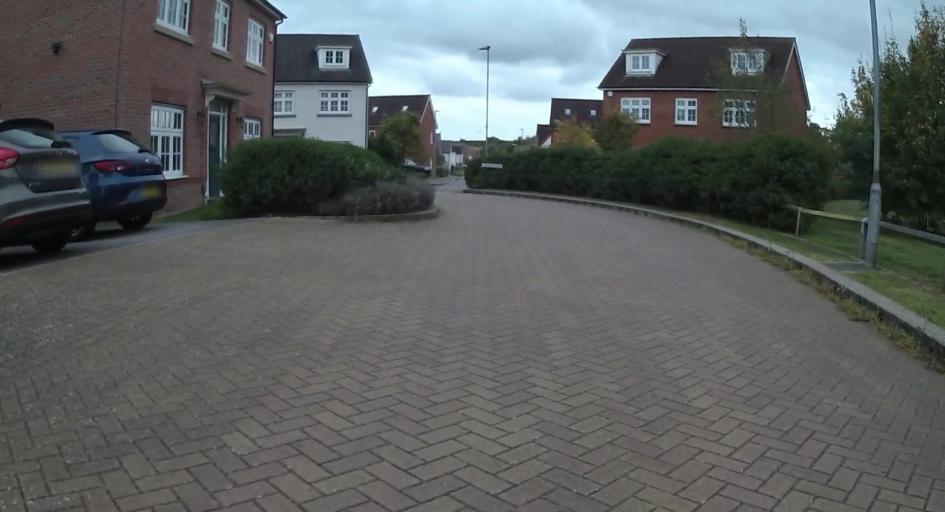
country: GB
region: England
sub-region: Bracknell Forest
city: Binfield
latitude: 51.4023
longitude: -0.7853
